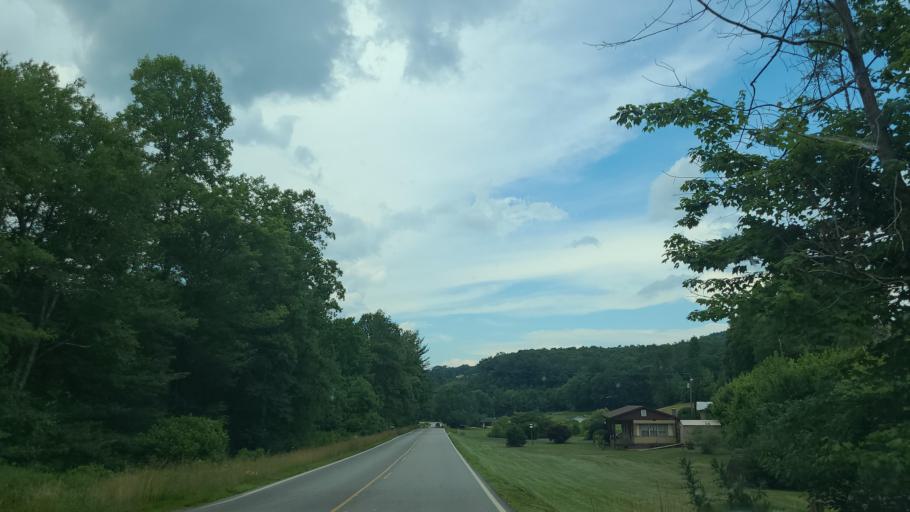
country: US
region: North Carolina
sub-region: Ashe County
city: Jefferson
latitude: 36.3930
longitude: -81.3273
